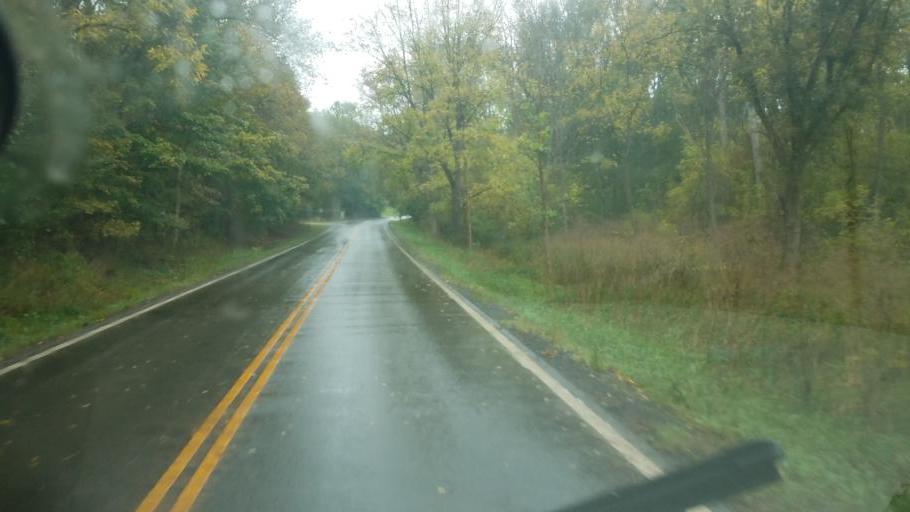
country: US
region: Ohio
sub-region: Richland County
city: Lincoln Heights
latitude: 40.7352
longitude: -82.3623
